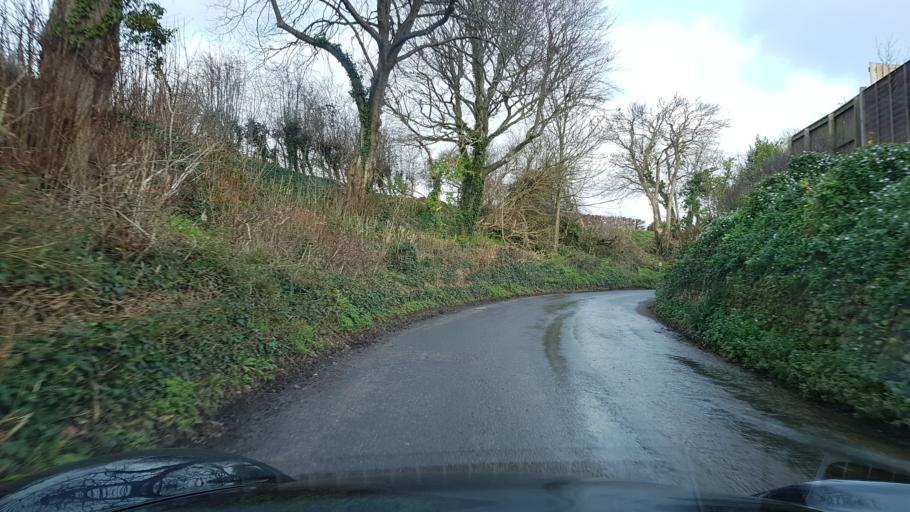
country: GB
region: England
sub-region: Dorset
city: Bridport
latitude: 50.7056
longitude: -2.7264
